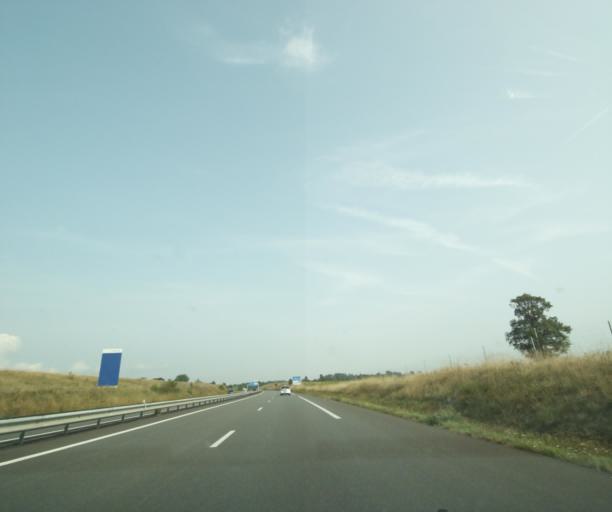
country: FR
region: Lower Normandy
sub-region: Departement de l'Orne
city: Valframbert
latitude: 48.4456
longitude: 0.1344
